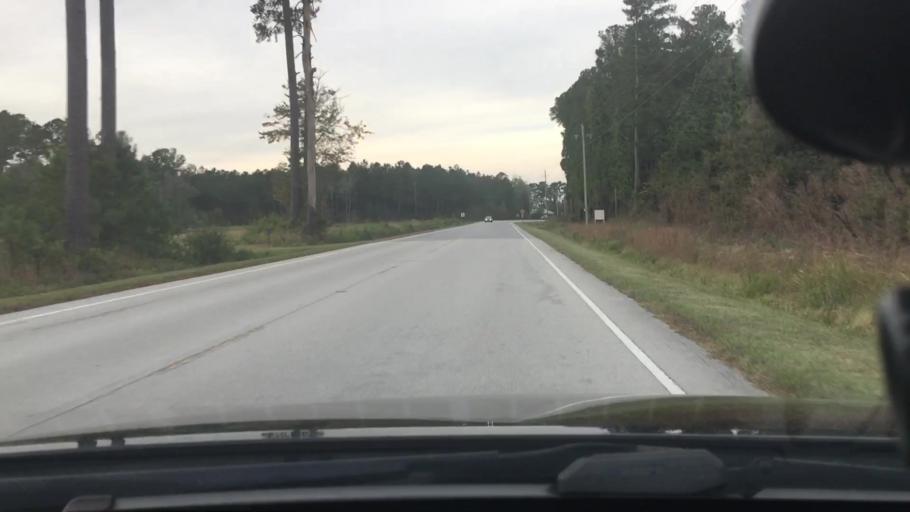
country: US
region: North Carolina
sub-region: Craven County
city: Vanceboro
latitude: 35.4149
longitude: -77.2526
